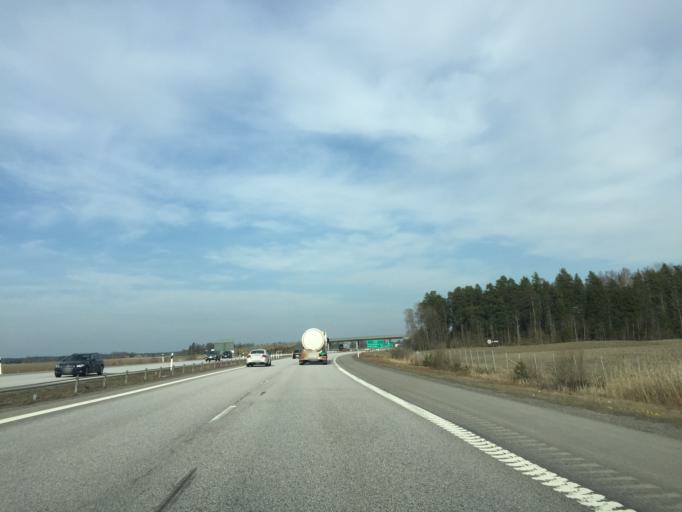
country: SE
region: Vaestmanland
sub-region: Arboga Kommun
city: Arboga
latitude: 59.4191
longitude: 15.7768
